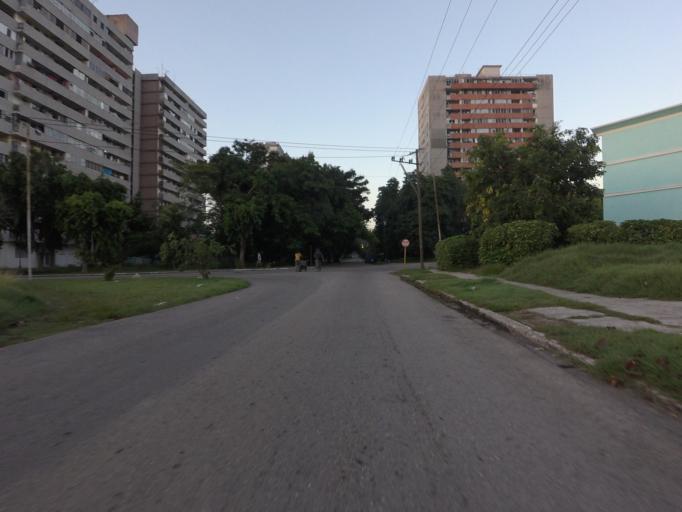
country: CU
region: La Habana
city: Havana
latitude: 23.1205
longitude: -82.3922
